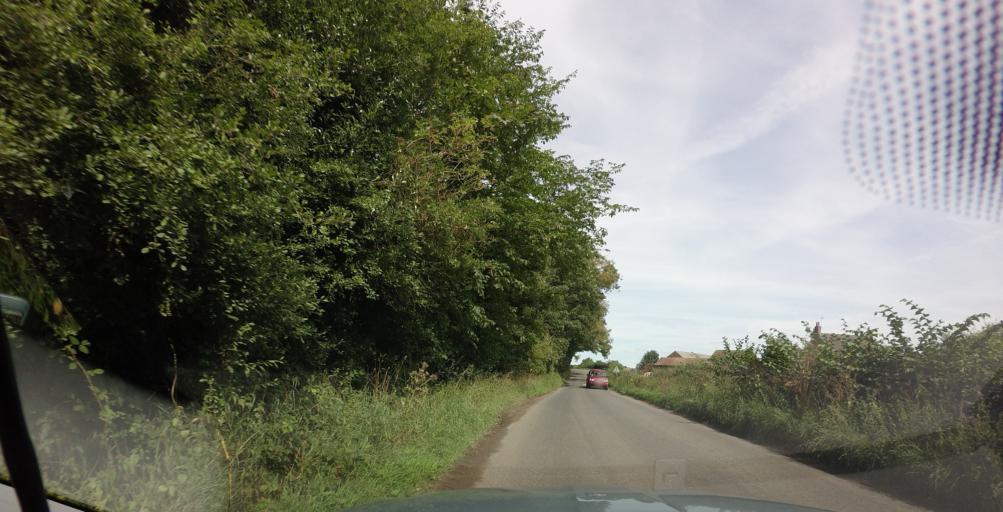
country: GB
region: England
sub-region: North Yorkshire
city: Ripon
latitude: 54.1000
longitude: -1.5143
